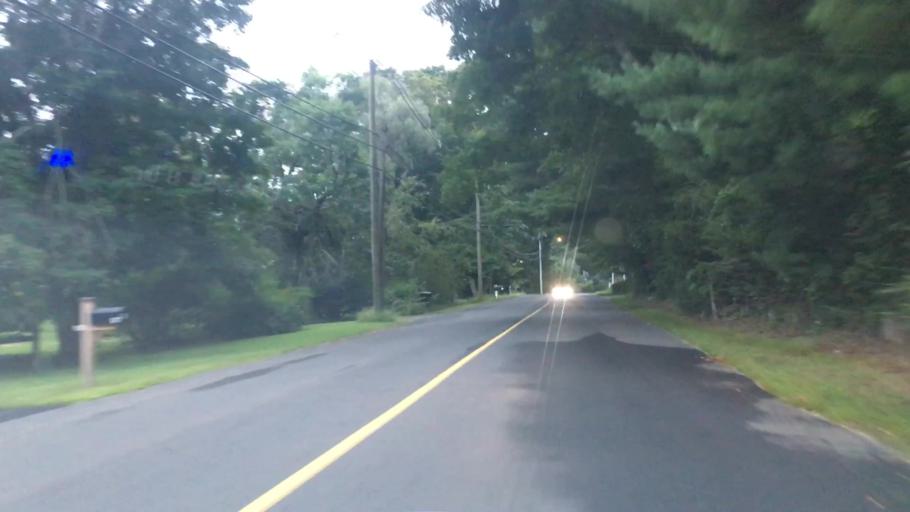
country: US
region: Connecticut
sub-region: Middlesex County
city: Essex Village
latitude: 41.3689
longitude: -72.3946
